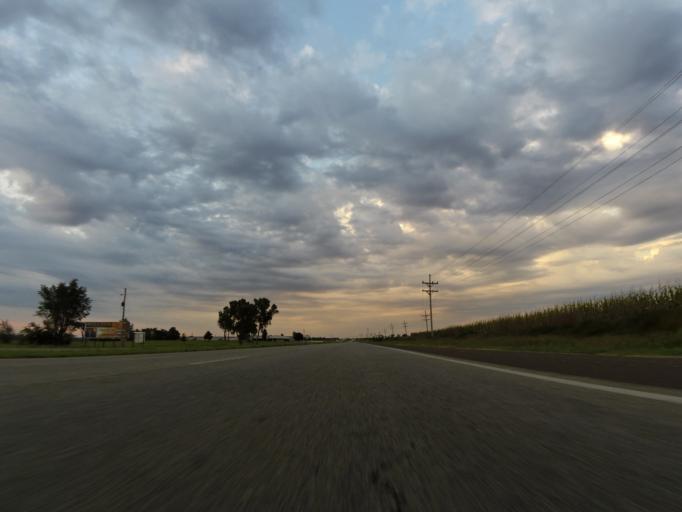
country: US
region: Kansas
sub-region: Reno County
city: South Hutchinson
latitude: 38.0057
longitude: -97.9405
